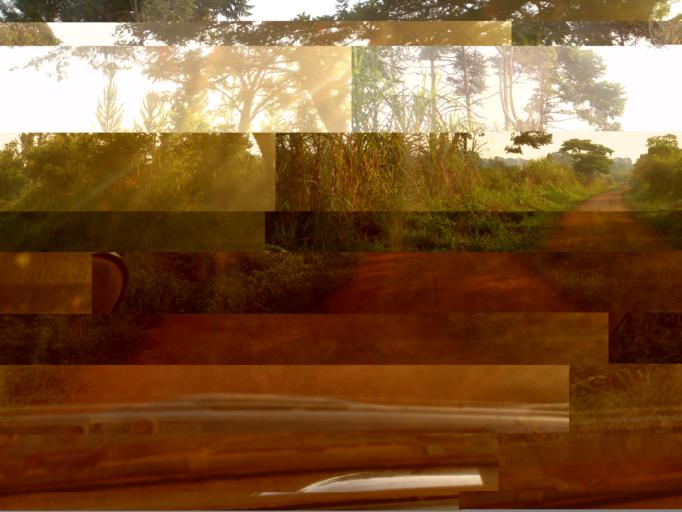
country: UG
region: Western Region
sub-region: Masindi District
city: Masindi
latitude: 1.7648
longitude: 31.8386
